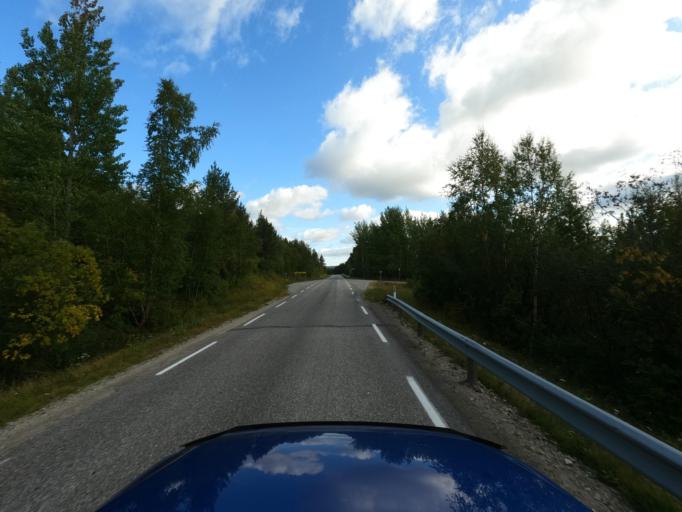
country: NO
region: Finnmark Fylke
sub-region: Karasjok
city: Karasjohka
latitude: 69.4548
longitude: 25.3898
